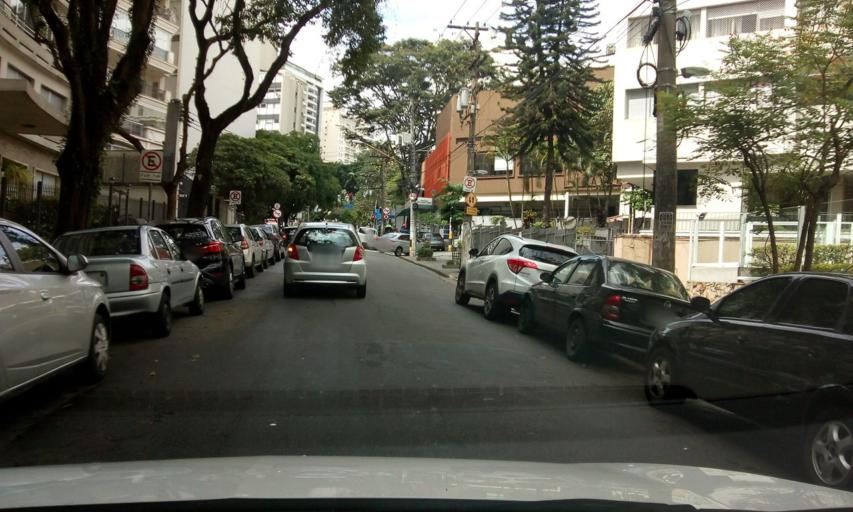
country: BR
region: Sao Paulo
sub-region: Sao Paulo
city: Sao Paulo
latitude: -23.5380
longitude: -46.6614
